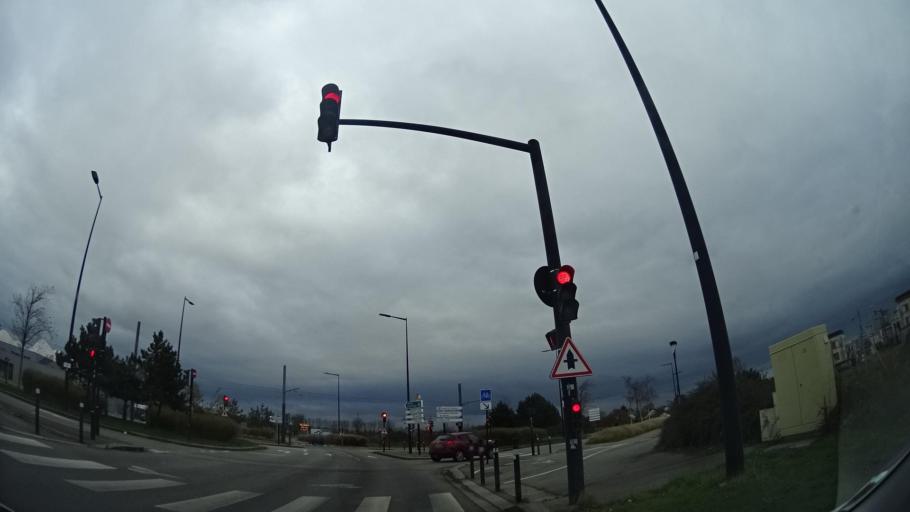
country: FR
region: Haute-Normandie
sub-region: Departement de la Seine-Maritime
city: Octeville-sur-Mer
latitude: 49.5294
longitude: 0.1069
